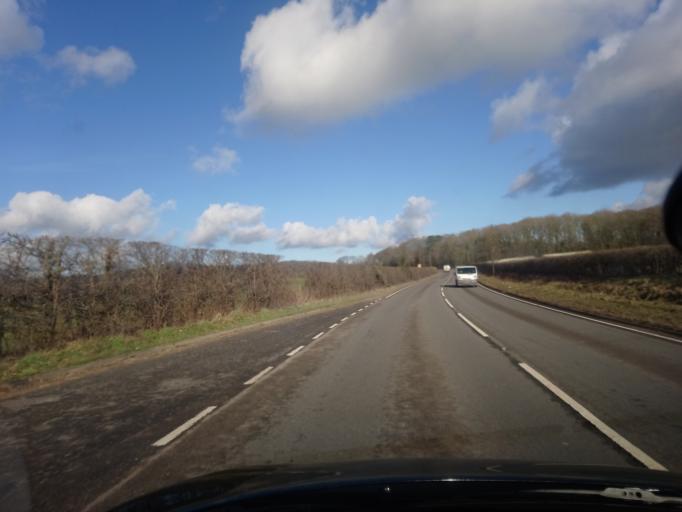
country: GB
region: England
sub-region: Shropshire
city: Clive
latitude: 52.7964
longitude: -2.7012
